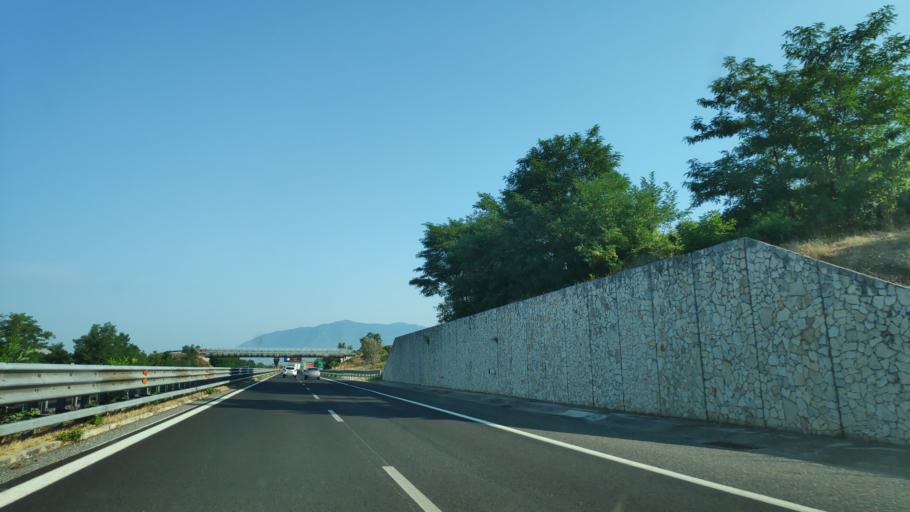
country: IT
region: Campania
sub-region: Provincia di Salerno
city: Buonabitacolo
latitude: 40.2798
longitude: 15.6532
